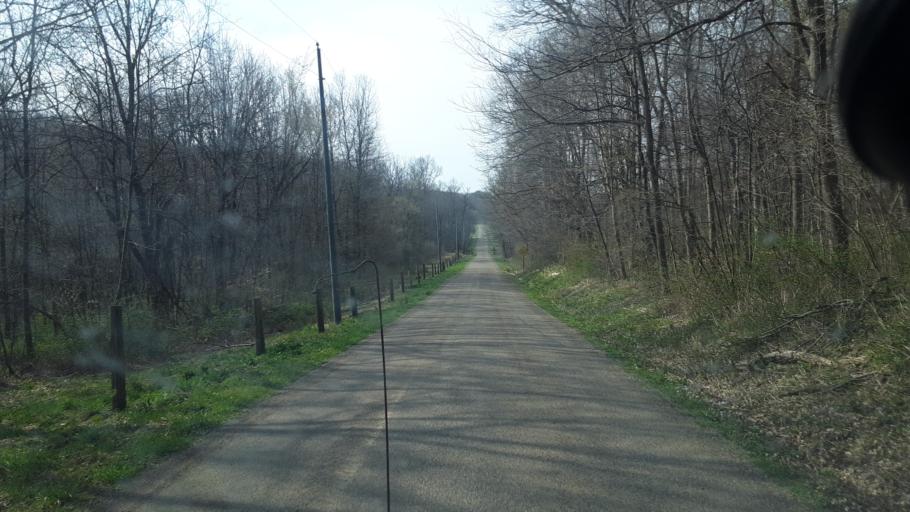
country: US
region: Ohio
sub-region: Ashland County
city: Loudonville
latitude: 40.5836
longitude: -82.3423
